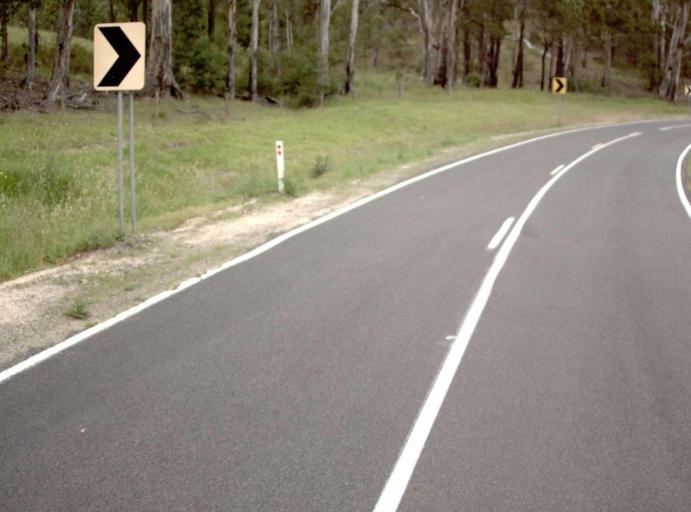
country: AU
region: New South Wales
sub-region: Bombala
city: Bombala
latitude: -37.4400
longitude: 149.1982
